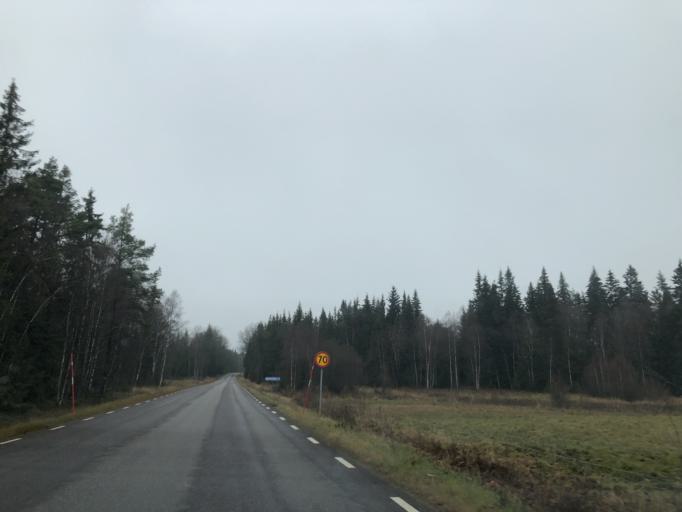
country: SE
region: Vaestra Goetaland
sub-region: Ulricehamns Kommun
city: Ulricehamn
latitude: 57.7259
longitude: 13.5487
